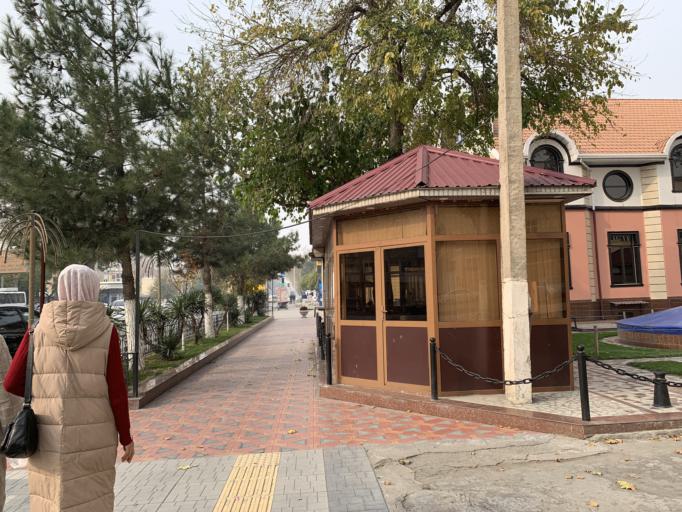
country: UZ
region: Fergana
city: Qo`qon
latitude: 40.5463
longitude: 70.9289
